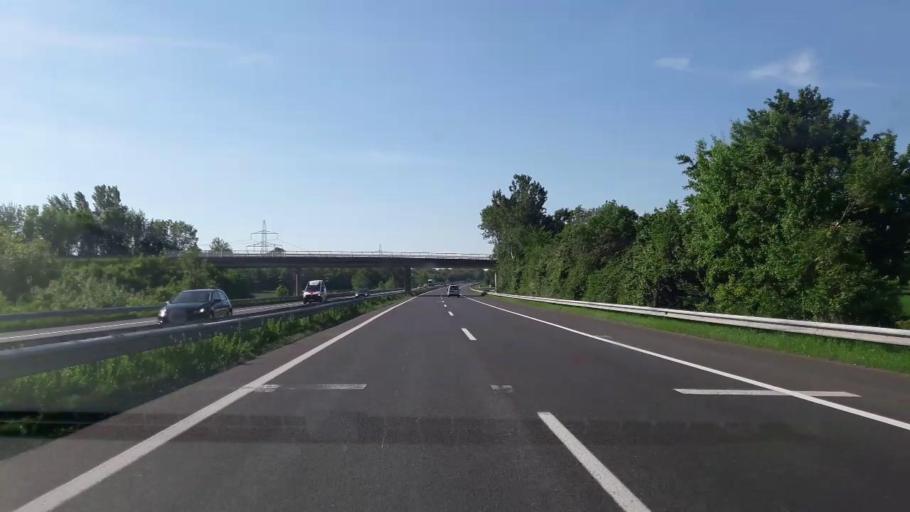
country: AT
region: Burgenland
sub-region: Eisenstadt-Umgebung
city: Wimpassing an der Leitha
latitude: 47.9083
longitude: 16.4109
